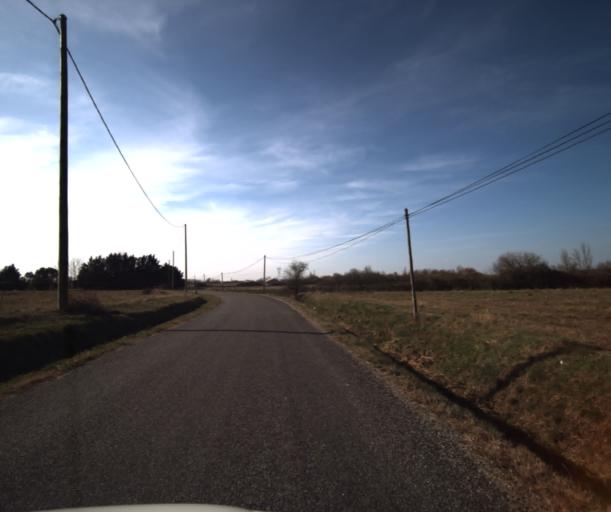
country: FR
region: Midi-Pyrenees
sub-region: Departement du Tarn-et-Garonne
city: Labastide-Saint-Pierre
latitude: 43.9258
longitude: 1.3397
